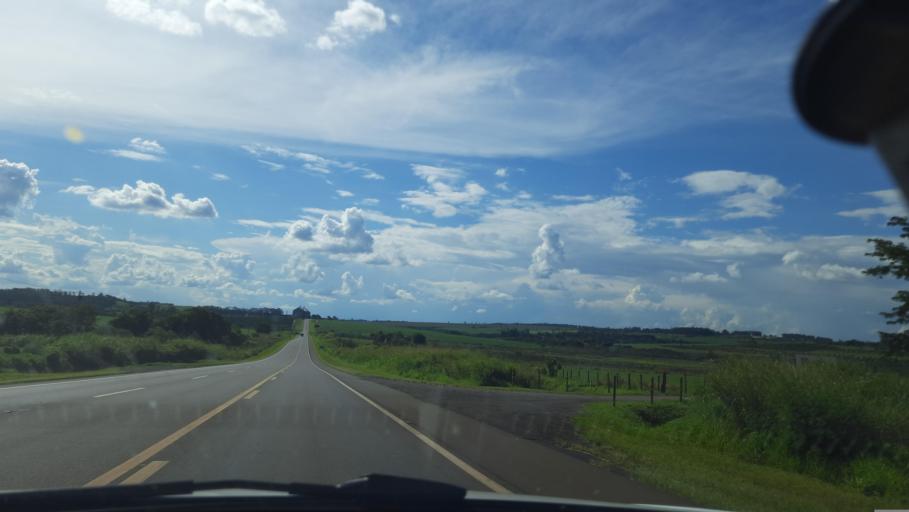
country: BR
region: Sao Paulo
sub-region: Casa Branca
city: Casa Branca
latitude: -21.8096
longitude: -46.9953
